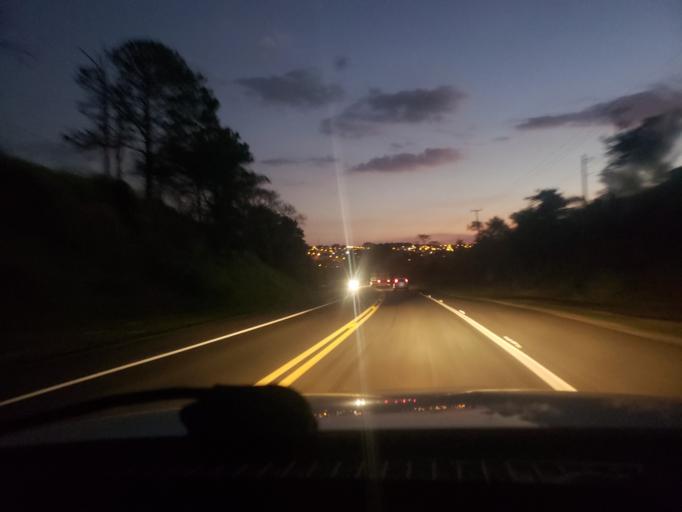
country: BR
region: Sao Paulo
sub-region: Conchal
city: Conchal
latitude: -22.3327
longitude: -47.1545
